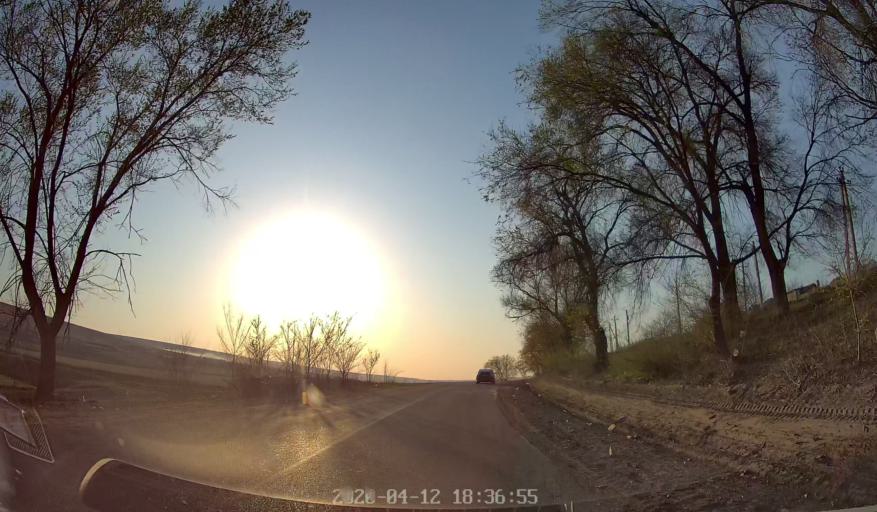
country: MD
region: Chisinau
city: Vadul lui Voda
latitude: 47.1179
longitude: 29.0221
